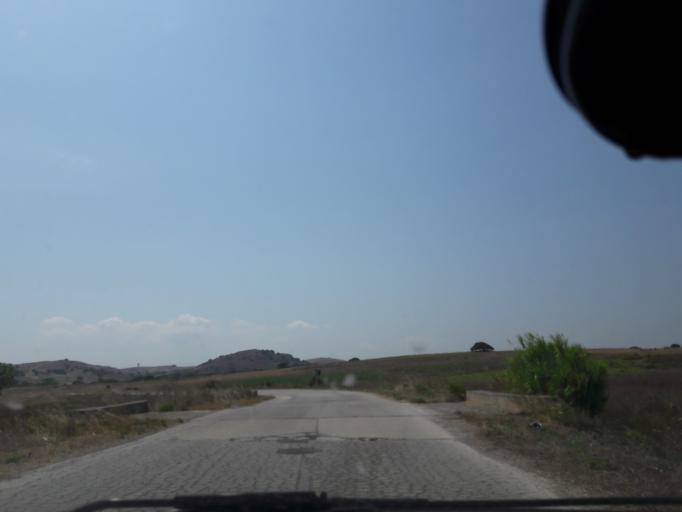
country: GR
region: North Aegean
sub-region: Nomos Lesvou
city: Myrina
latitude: 39.9165
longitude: 25.3204
